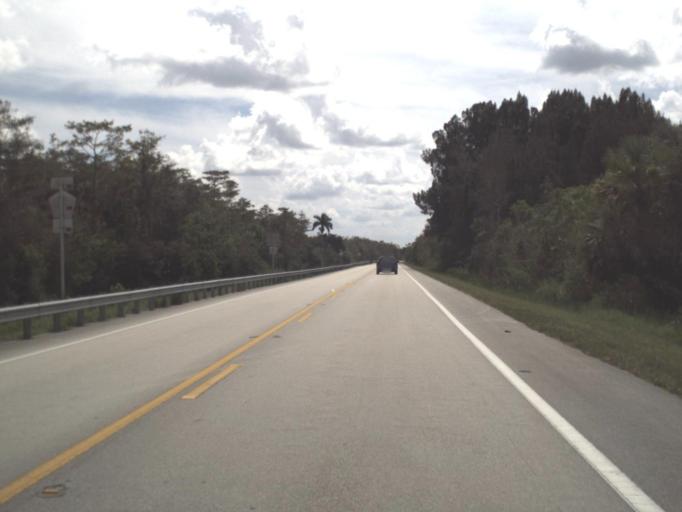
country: US
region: Florida
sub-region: Collier County
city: Lely Resort
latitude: 25.9444
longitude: -81.3578
